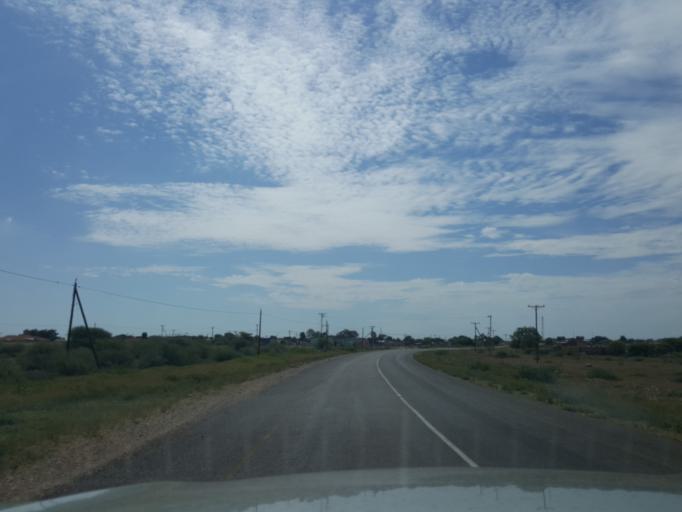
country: BW
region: Kweneng
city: Letlhakeng
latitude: -24.1141
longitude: 25.0372
